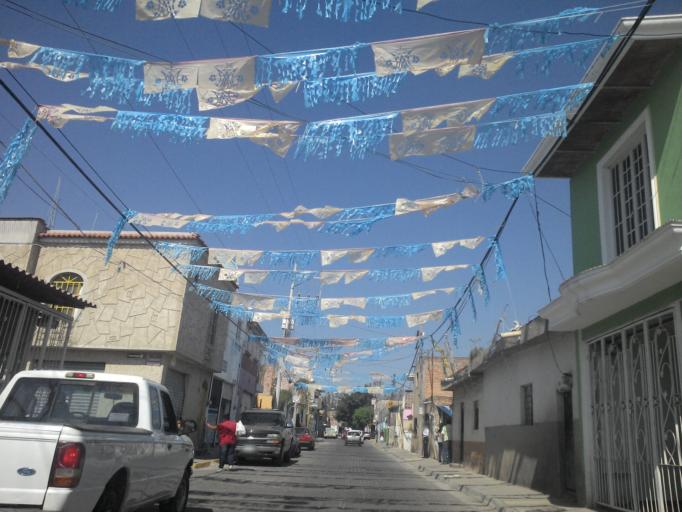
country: MX
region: Jalisco
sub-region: San Pedro Tlaquepaque
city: Paseo del Prado
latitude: 20.5895
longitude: -103.3874
